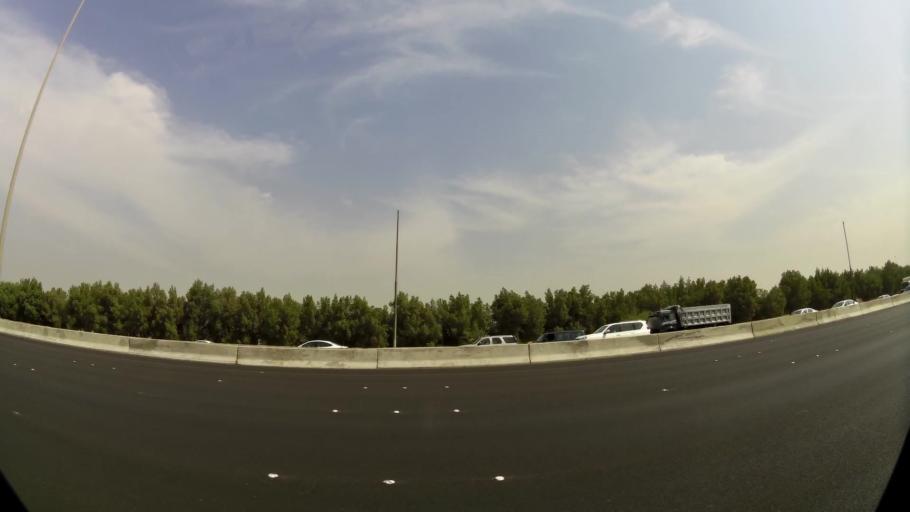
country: KW
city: Bayan
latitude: 29.2831
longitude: 48.0331
